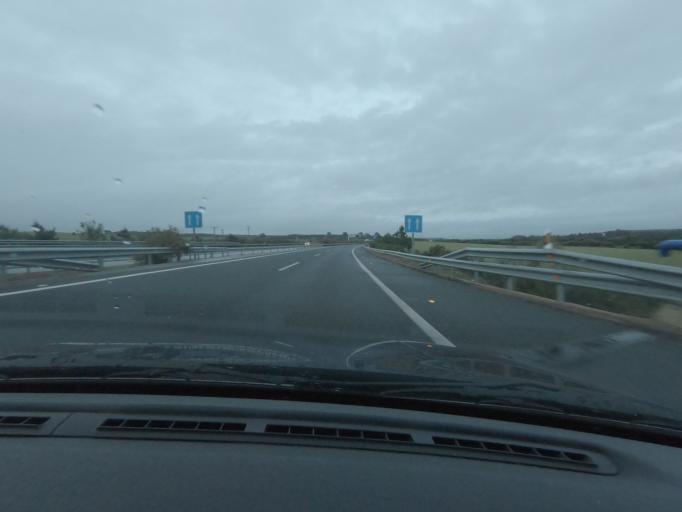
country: ES
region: Extremadura
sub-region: Provincia de Badajoz
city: Aljucen
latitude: 39.0491
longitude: -6.3362
